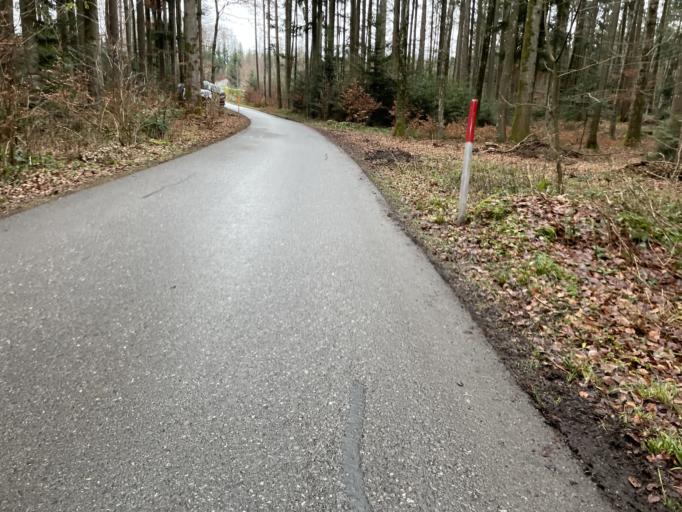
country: CH
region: Bern
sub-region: Bern-Mittelland District
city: Toffen
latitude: 46.8630
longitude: 7.5208
